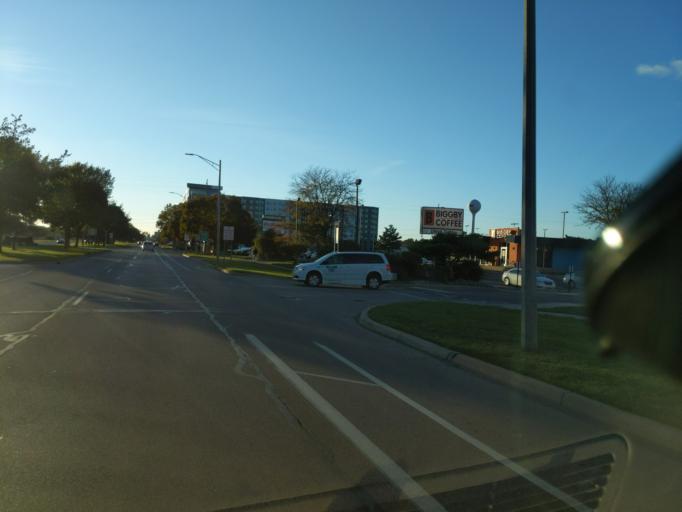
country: US
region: Michigan
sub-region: Ingham County
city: East Lansing
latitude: 42.7336
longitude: -84.5014
